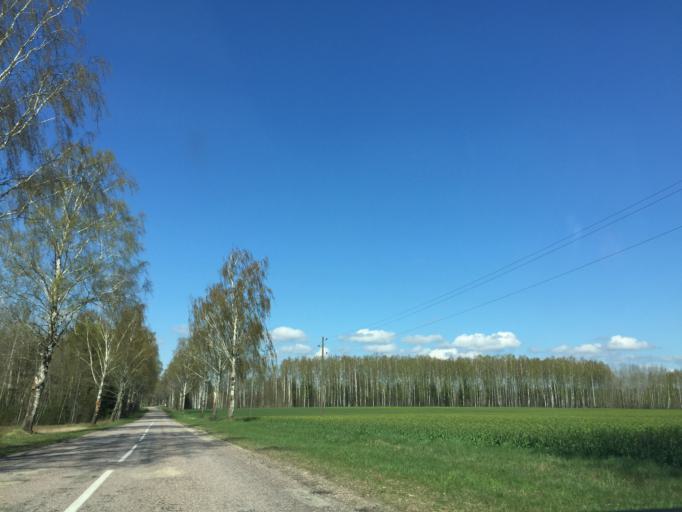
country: LV
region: Strenci
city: Seda
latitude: 57.5538
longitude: 25.8255
